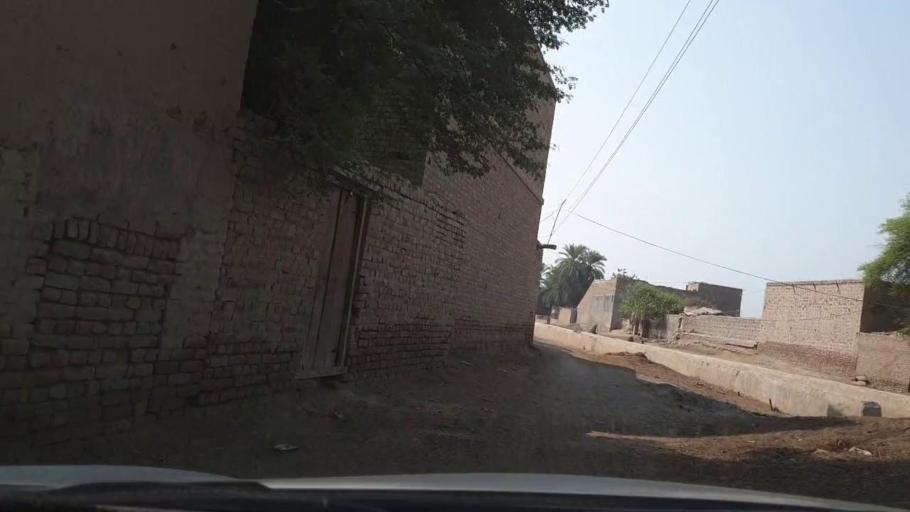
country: PK
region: Sindh
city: Larkana
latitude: 27.4659
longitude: 68.2431
